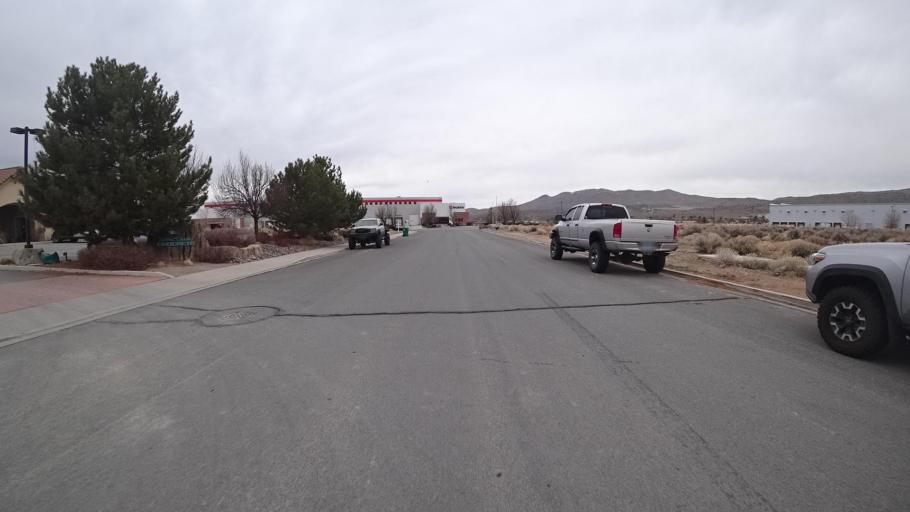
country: US
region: Nevada
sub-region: Washoe County
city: Spanish Springs
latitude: 39.6734
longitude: -119.7079
